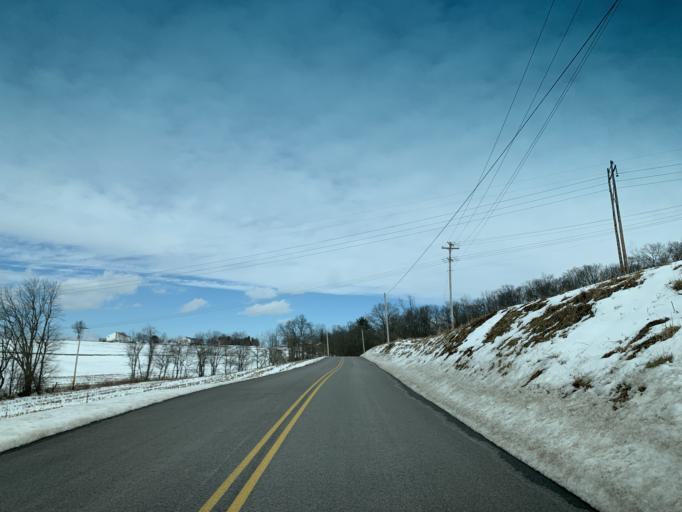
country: US
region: Pennsylvania
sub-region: York County
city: Shrewsbury
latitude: 39.7683
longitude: -76.6496
